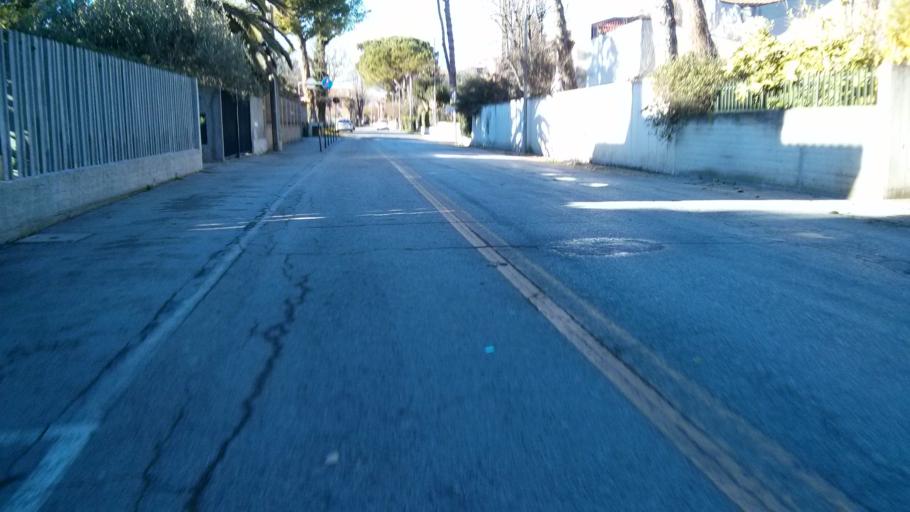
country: IT
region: The Marches
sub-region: Provincia di Pesaro e Urbino
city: Fano
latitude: 43.8460
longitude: 13.0071
